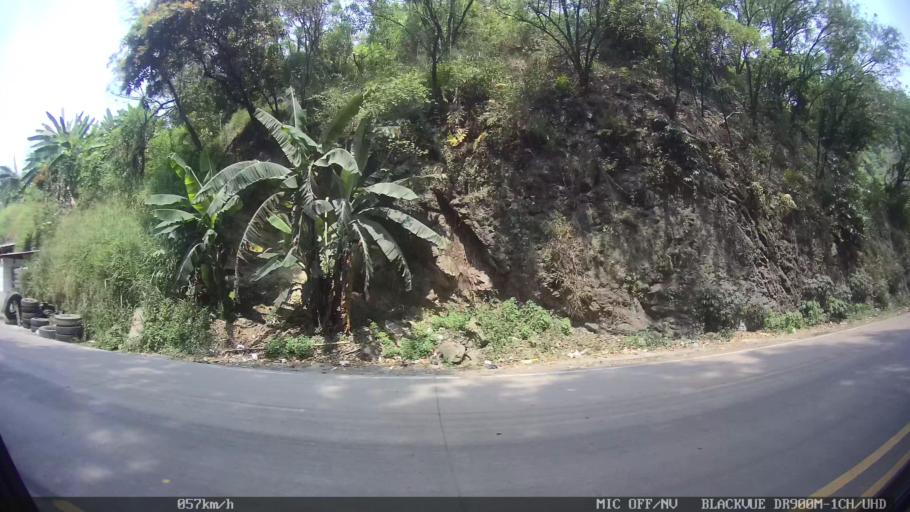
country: ID
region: Banten
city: Curug
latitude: -5.9472
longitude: 106.0039
